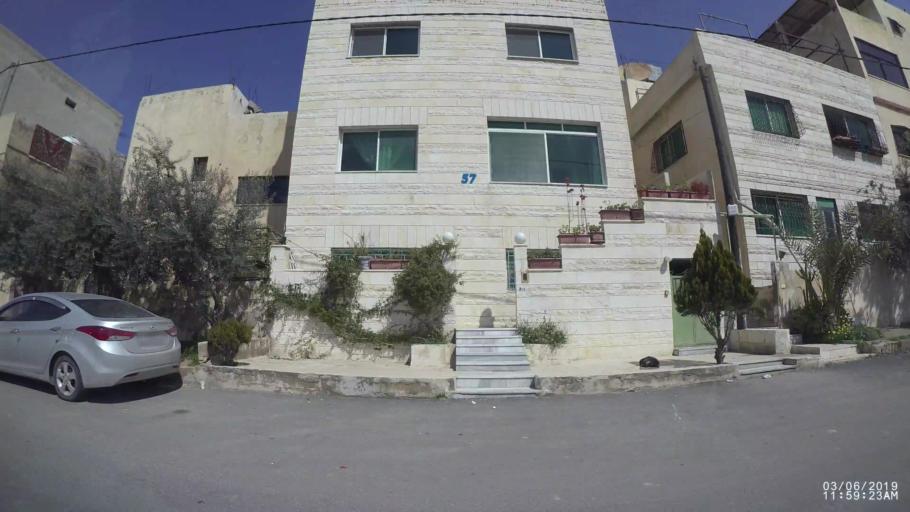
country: JO
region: Zarqa
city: Russeifa
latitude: 31.9873
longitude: 36.0170
